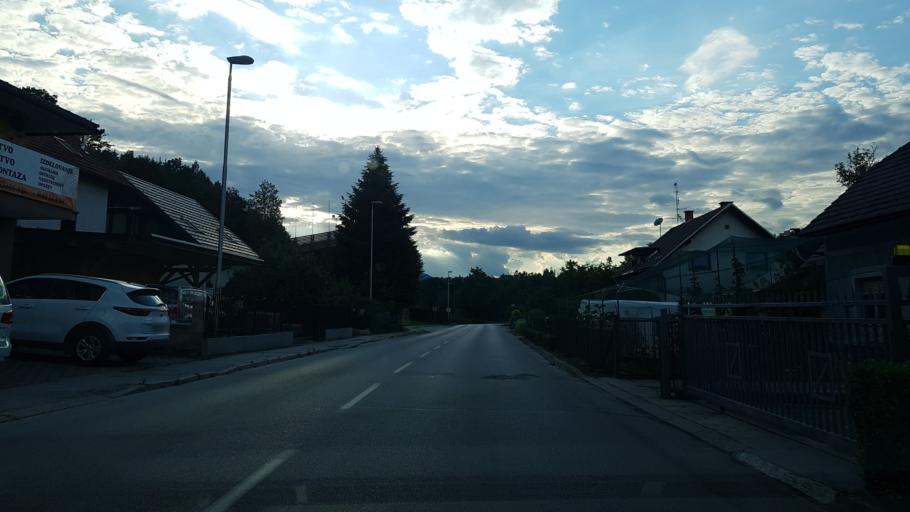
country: SI
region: Kranj
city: Kranj
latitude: 46.2486
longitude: 14.3340
